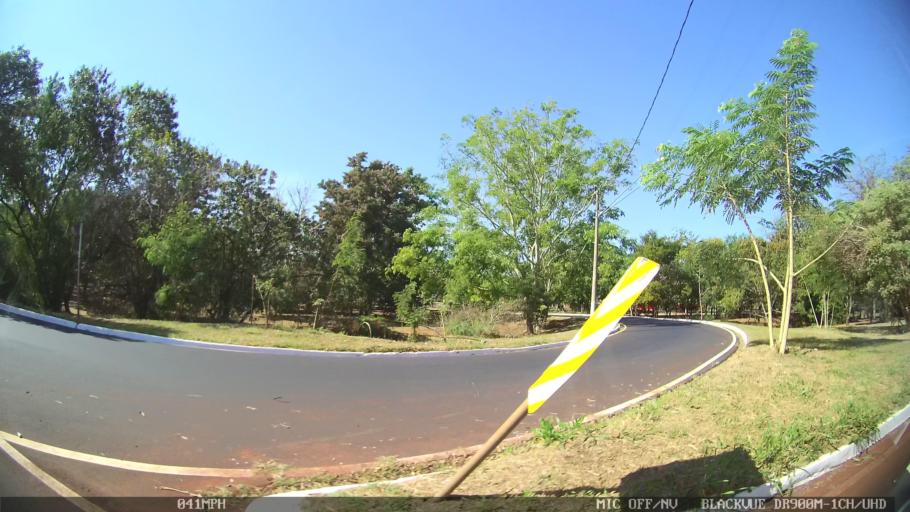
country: BR
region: Sao Paulo
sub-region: Ribeirao Preto
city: Ribeirao Preto
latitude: -21.2256
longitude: -47.7683
